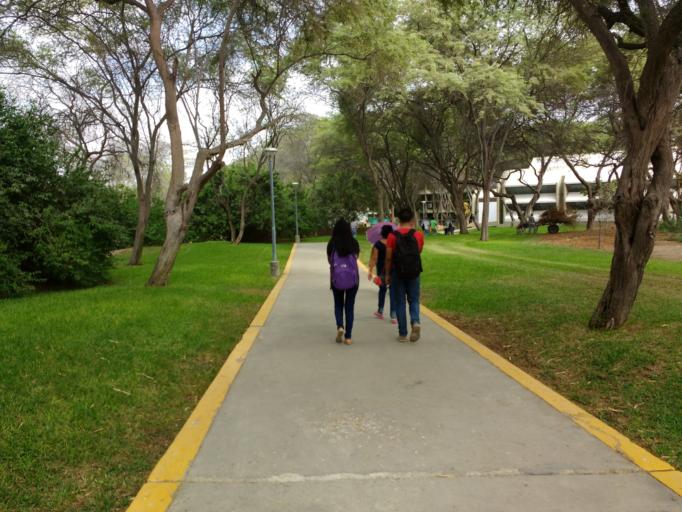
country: PE
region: Piura
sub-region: Provincia de Piura
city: Piura
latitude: -5.1785
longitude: -80.6345
